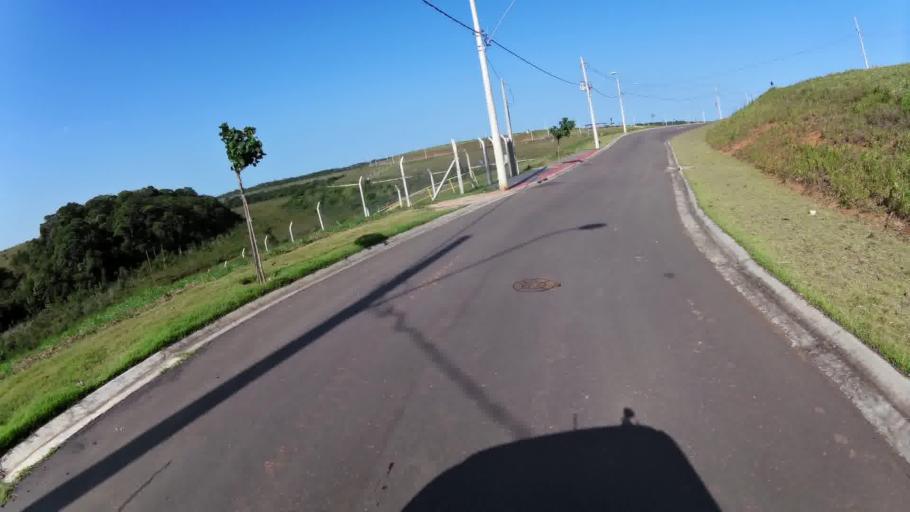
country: BR
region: Espirito Santo
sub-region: Guarapari
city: Guarapari
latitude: -20.7120
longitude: -40.5342
